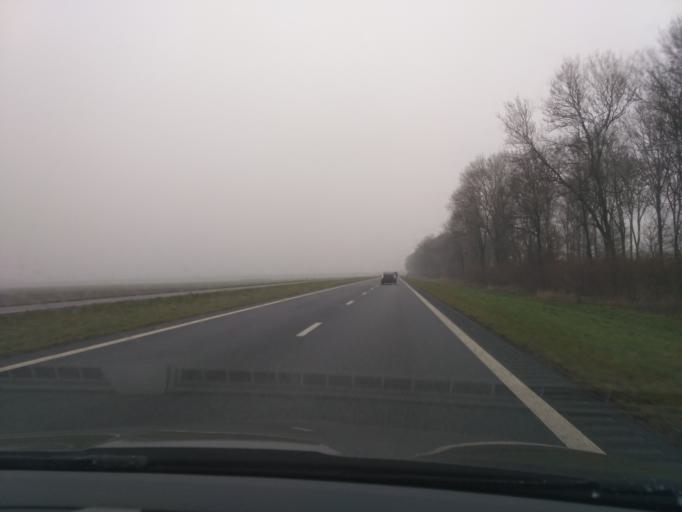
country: NL
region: Flevoland
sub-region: Gemeente Zeewolde
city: Zeewolde
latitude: 52.3694
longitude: 5.5353
